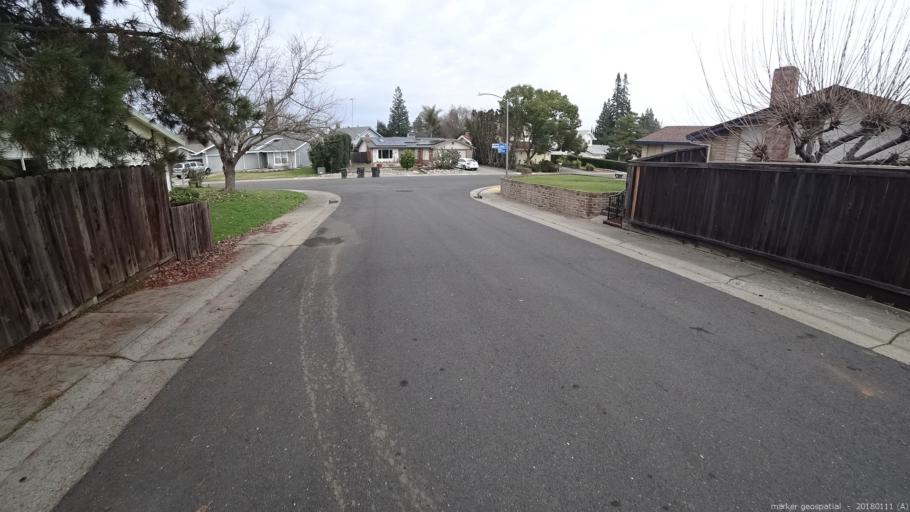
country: US
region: California
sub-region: Sacramento County
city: Fair Oaks
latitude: 38.6180
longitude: -121.2807
